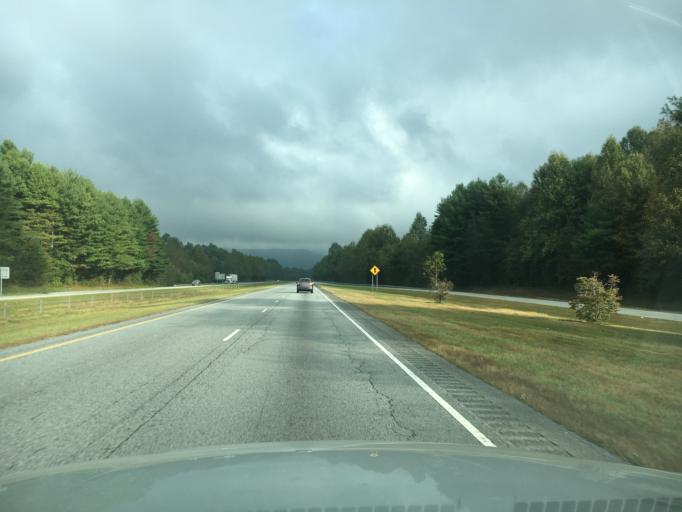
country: US
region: North Carolina
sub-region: Henderson County
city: Flat Rock
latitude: 35.1892
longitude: -82.4489
